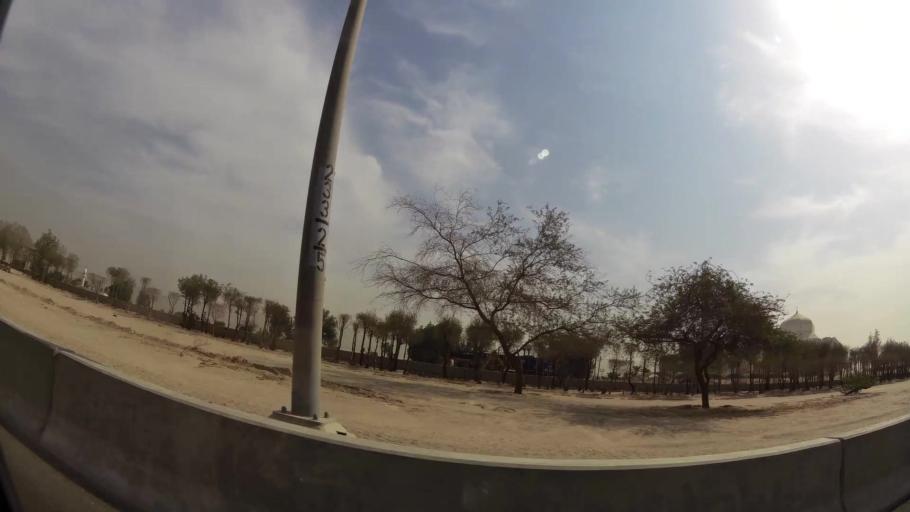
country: KW
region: Al Farwaniyah
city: Janub as Surrah
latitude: 29.2698
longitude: 47.9708
